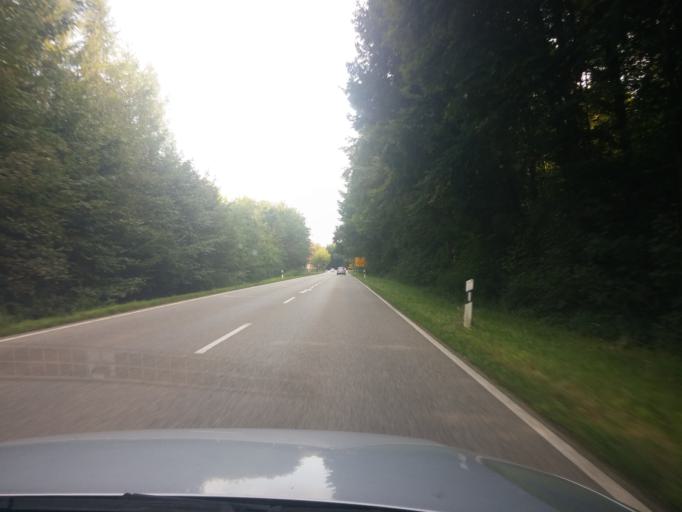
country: DE
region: Bavaria
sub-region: Upper Bavaria
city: Grasbrunn
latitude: 48.0520
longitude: 11.7607
